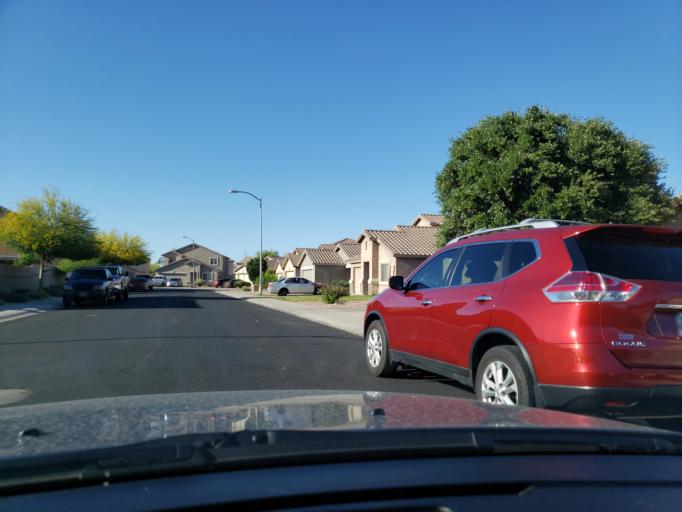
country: US
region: Arizona
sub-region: Maricopa County
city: Youngtown
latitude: 33.5715
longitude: -112.3077
